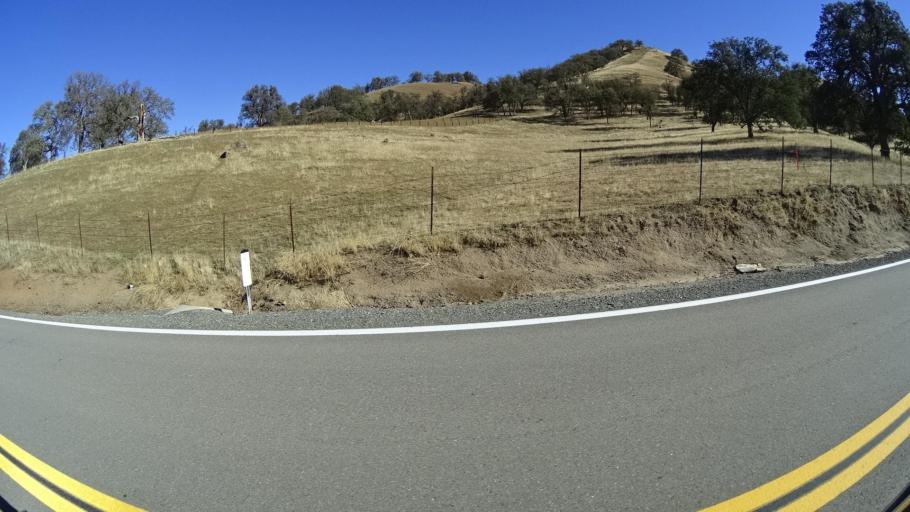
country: US
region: California
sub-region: Kern County
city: Alta Sierra
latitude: 35.7234
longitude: -118.6980
